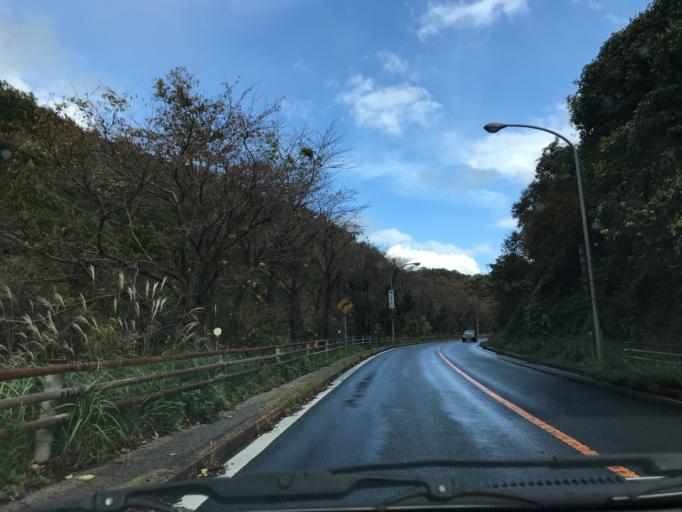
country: JP
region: Shimane
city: Sakaiminato
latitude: 35.5518
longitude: 133.2386
